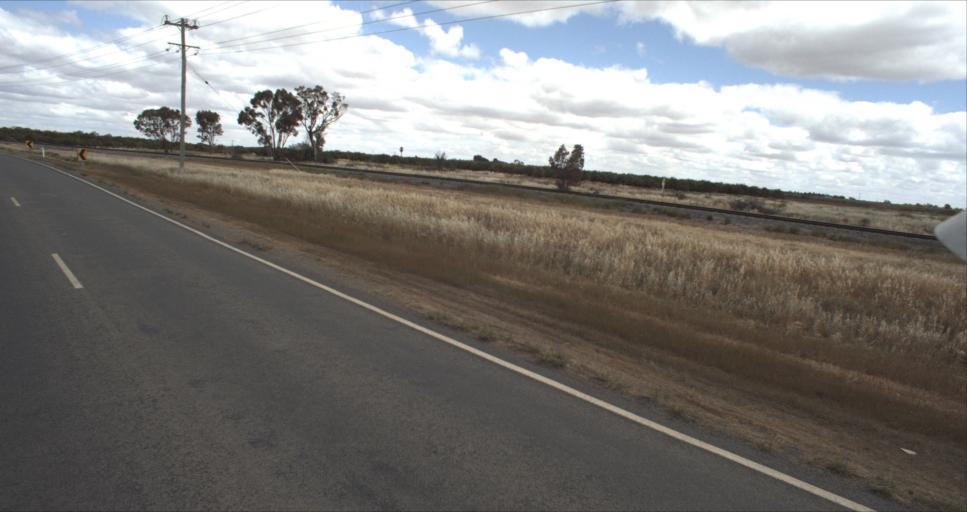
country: AU
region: New South Wales
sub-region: Leeton
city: Leeton
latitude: -34.5753
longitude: 146.3952
